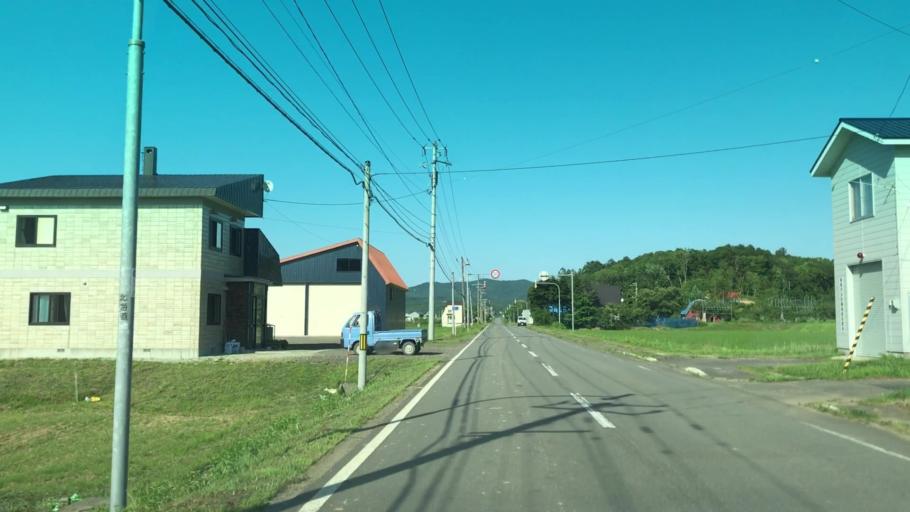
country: JP
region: Hokkaido
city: Yoichi
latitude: 43.0380
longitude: 140.7871
